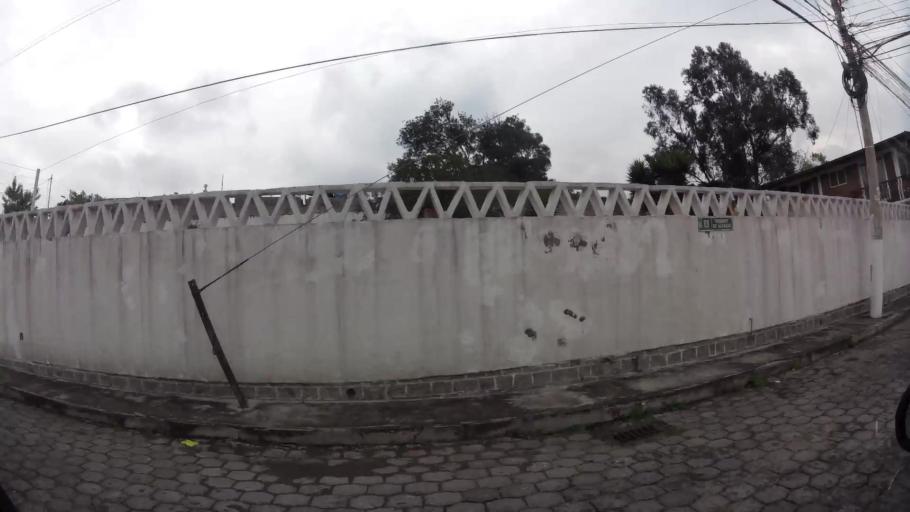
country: EC
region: Pichincha
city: Sangolqui
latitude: -0.2990
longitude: -78.4724
